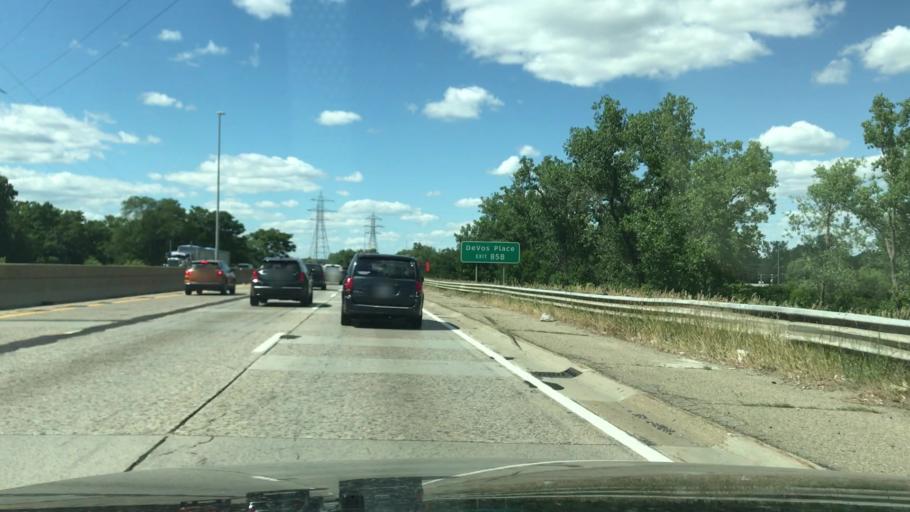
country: US
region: Michigan
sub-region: Kent County
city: Wyoming
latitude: 42.9210
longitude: -85.6809
